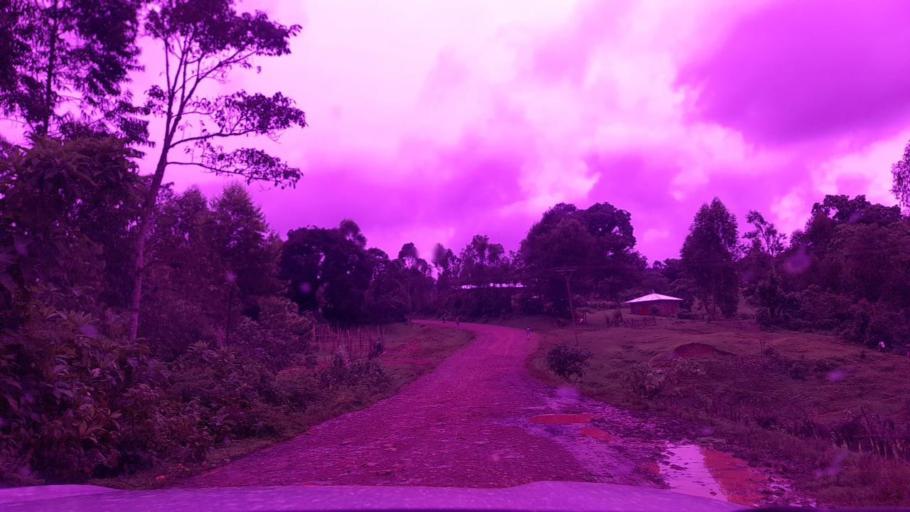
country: ET
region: Southern Nations, Nationalities, and People's Region
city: Tippi
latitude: 7.5875
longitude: 35.7668
